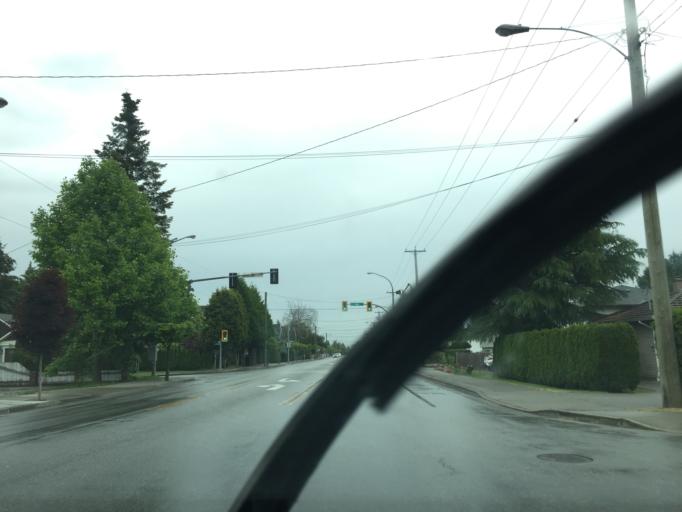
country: CA
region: British Columbia
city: Richmond
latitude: 49.1408
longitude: -123.1207
